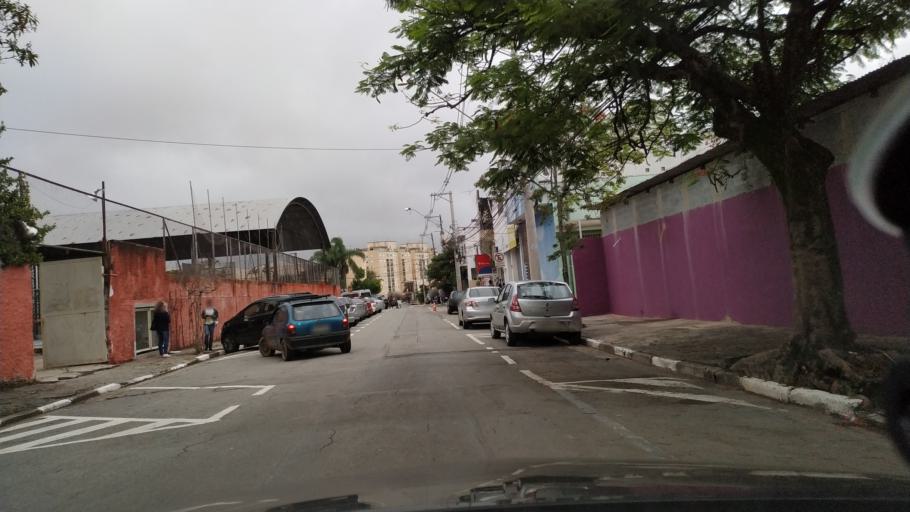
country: BR
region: Sao Paulo
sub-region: Barueri
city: Barueri
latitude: -23.5031
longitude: -46.8710
